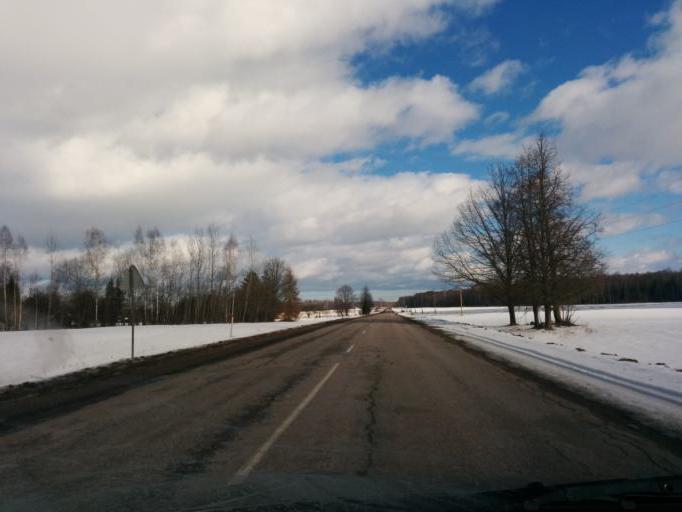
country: LV
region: Gulbenes Rajons
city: Gulbene
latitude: 57.1779
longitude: 26.8214
